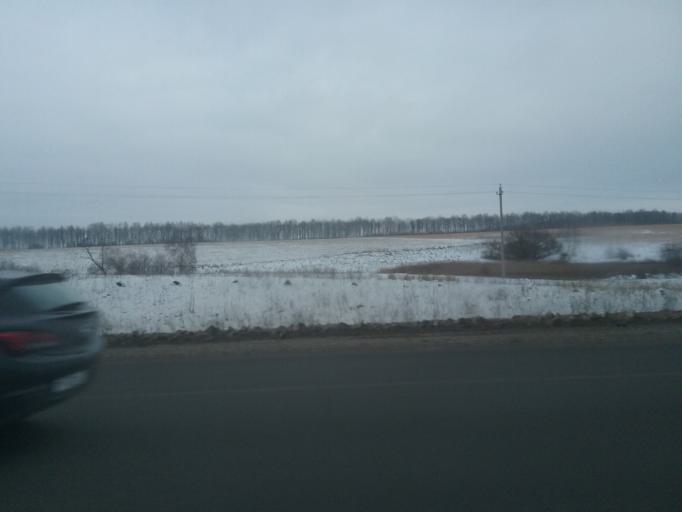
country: RU
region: Tula
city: Bolokhovo
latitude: 54.0349
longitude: 37.8772
